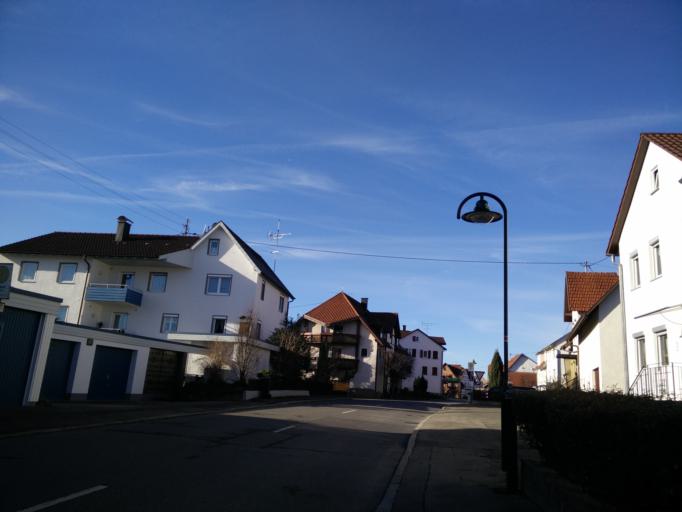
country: DE
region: Baden-Wuerttemberg
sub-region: Tuebingen Region
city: Gomaringen
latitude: 48.4727
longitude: 9.0875
